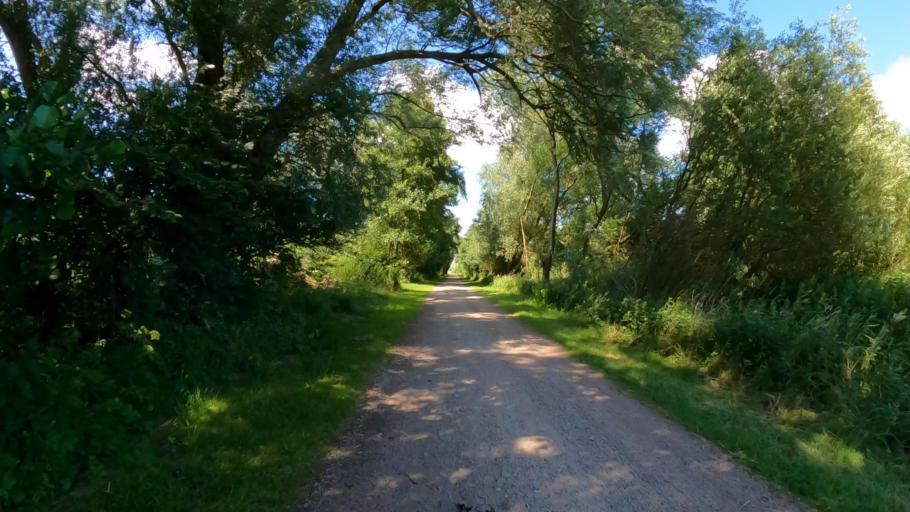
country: DE
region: Lower Saxony
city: Neu Wulmstorf
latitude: 53.4853
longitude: 9.8557
